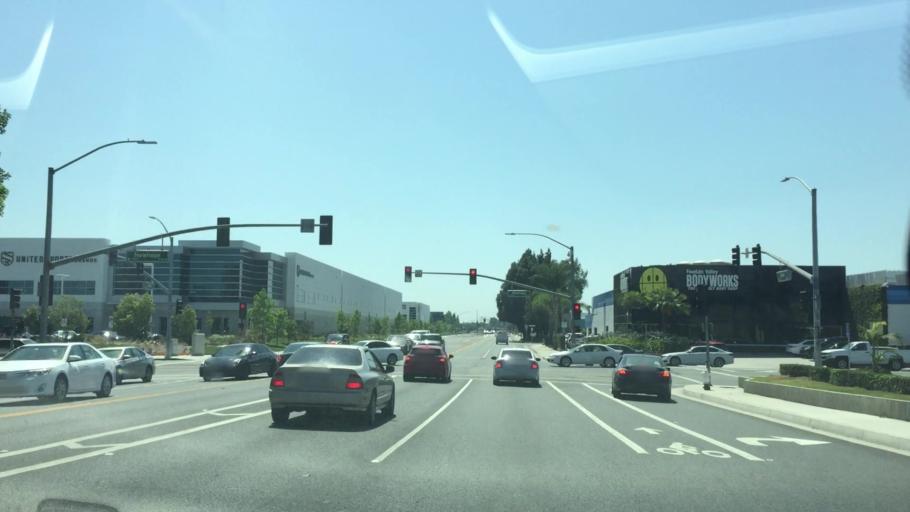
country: US
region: California
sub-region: Orange County
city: Fountain Valley
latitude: 33.7092
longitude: -117.9278
